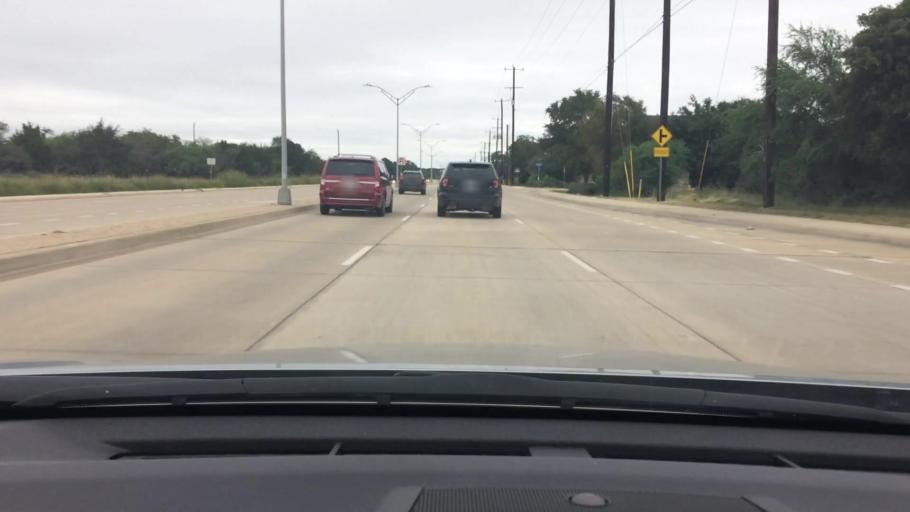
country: US
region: Texas
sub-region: Bexar County
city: Hollywood Park
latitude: 29.6187
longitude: -98.4227
